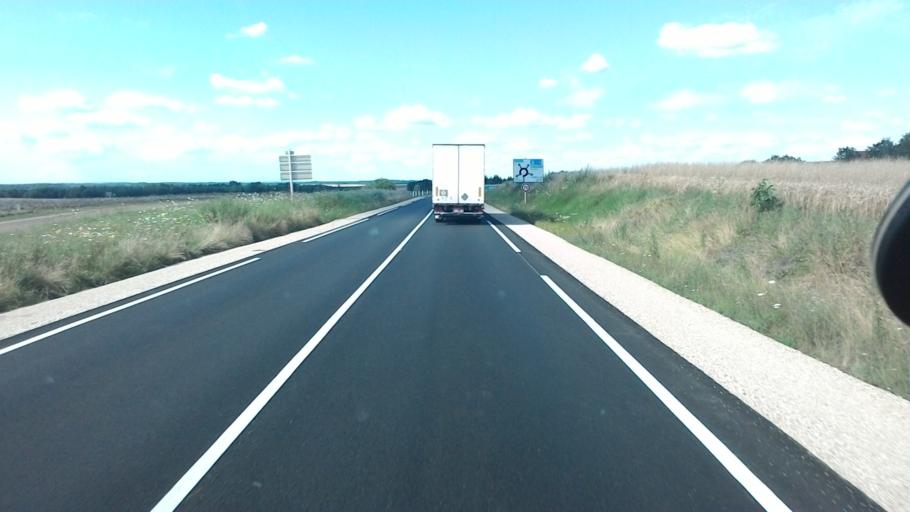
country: FR
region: Franche-Comte
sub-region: Departement de la Haute-Saone
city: Marnay
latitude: 47.3387
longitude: 5.6983
